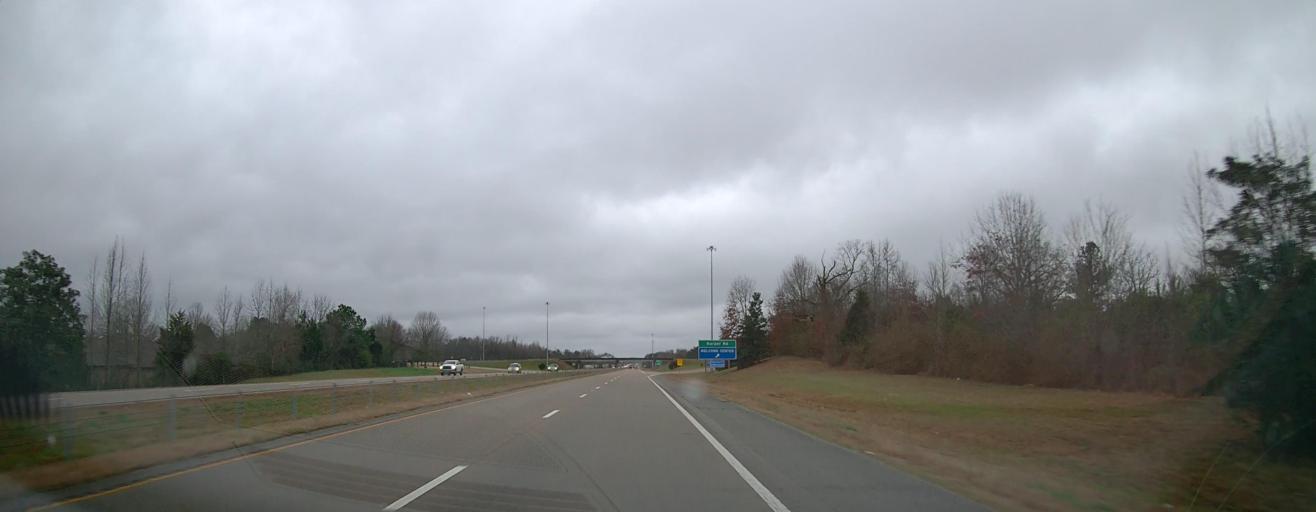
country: US
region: Mississippi
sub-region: Alcorn County
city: Corinth
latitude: 34.9132
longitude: -88.5433
